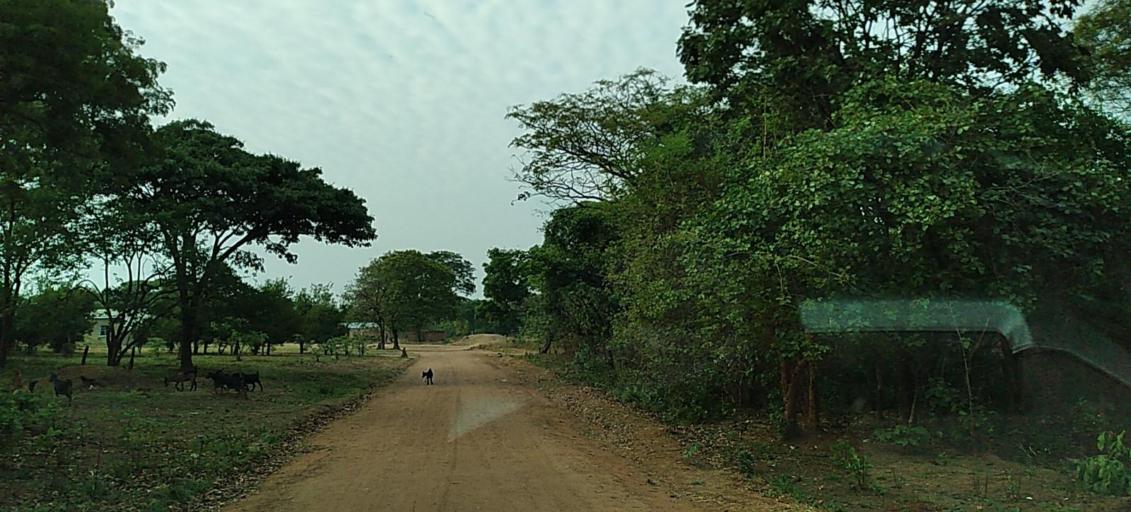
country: ZM
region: Copperbelt
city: Kalulushi
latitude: -12.9099
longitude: 27.6891
